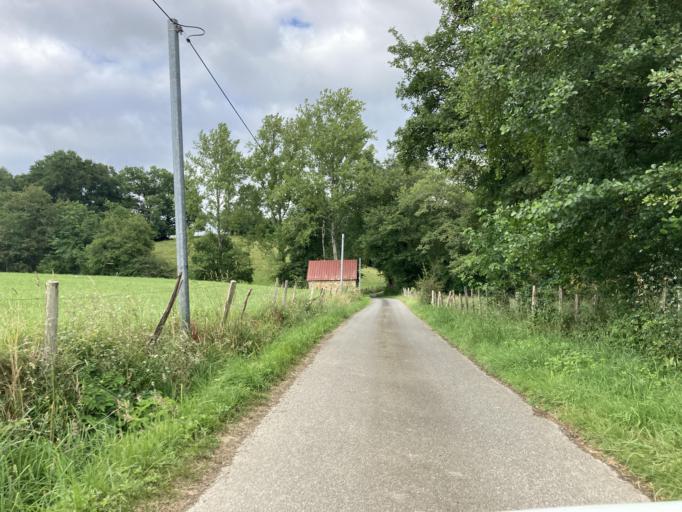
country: FR
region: Aquitaine
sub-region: Departement des Pyrenees-Atlantiques
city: Ledeuix
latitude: 43.2592
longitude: -0.6393
